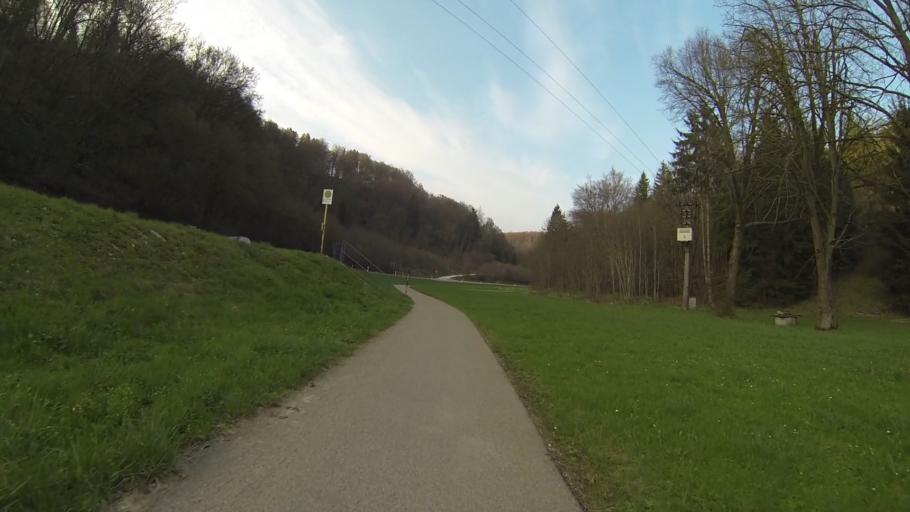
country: DE
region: Baden-Wuerttemberg
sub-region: Regierungsbezirk Stuttgart
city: Nattheim
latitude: 48.6958
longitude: 10.2009
